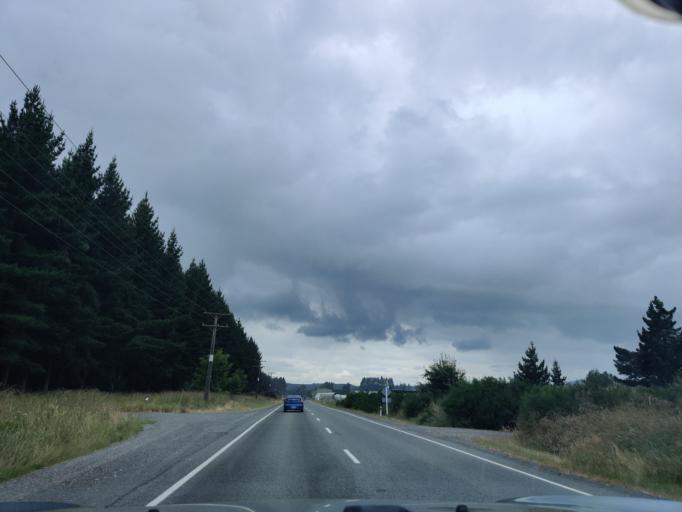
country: NZ
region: Manawatu-Wanganui
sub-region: Ruapehu District
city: Waiouru
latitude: -39.4673
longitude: 175.5936
